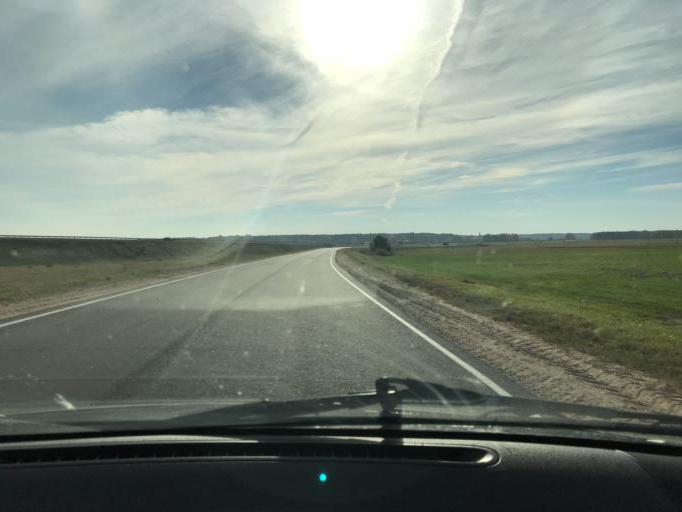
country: BY
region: Brest
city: Asnyezhytsy
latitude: 52.1854
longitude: 26.0775
